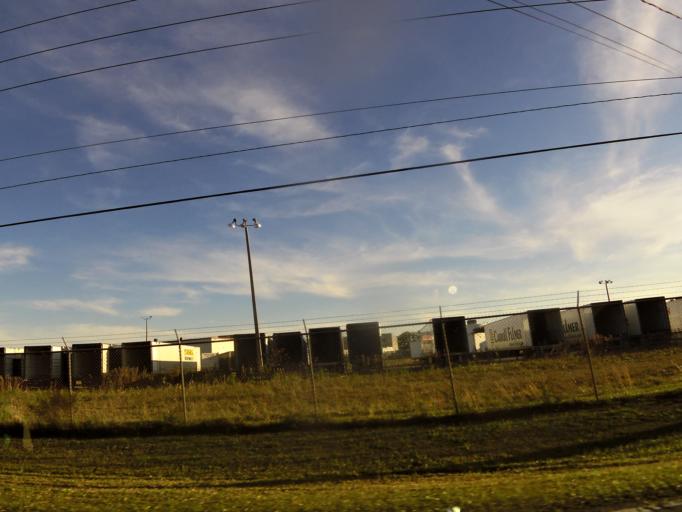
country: US
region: Florida
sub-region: Duval County
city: Jacksonville
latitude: 30.4626
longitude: -81.6408
